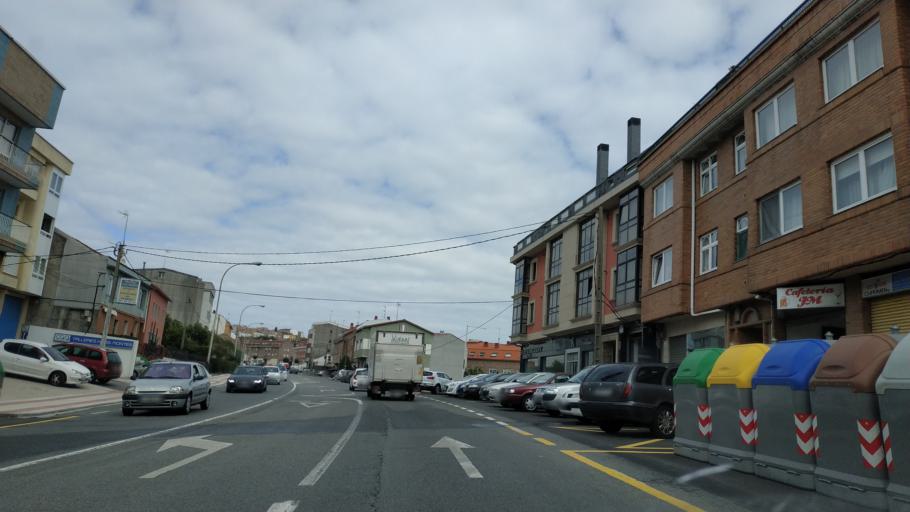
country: ES
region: Galicia
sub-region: Provincia da Coruna
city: Arteixo
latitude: 43.3185
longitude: -8.4752
